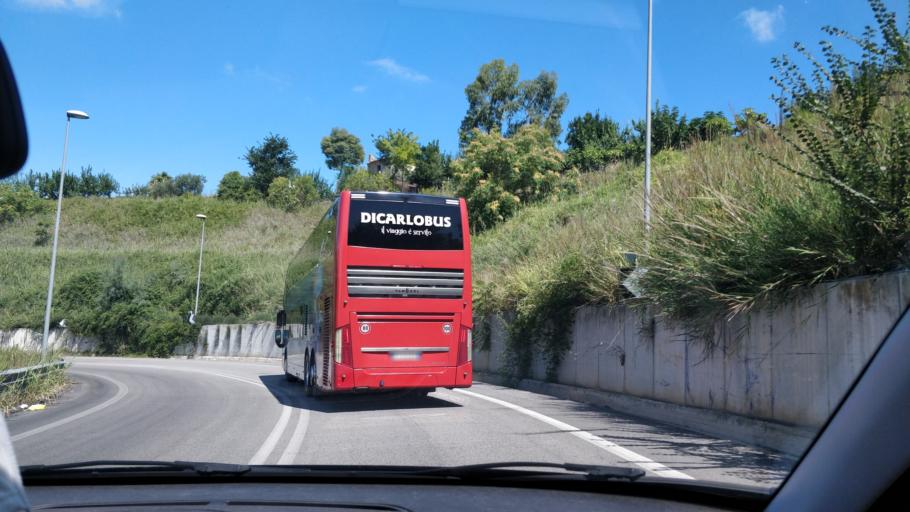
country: IT
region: Abruzzo
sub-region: Provincia di Chieti
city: Francavilla al Mare
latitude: 42.4057
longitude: 14.3036
